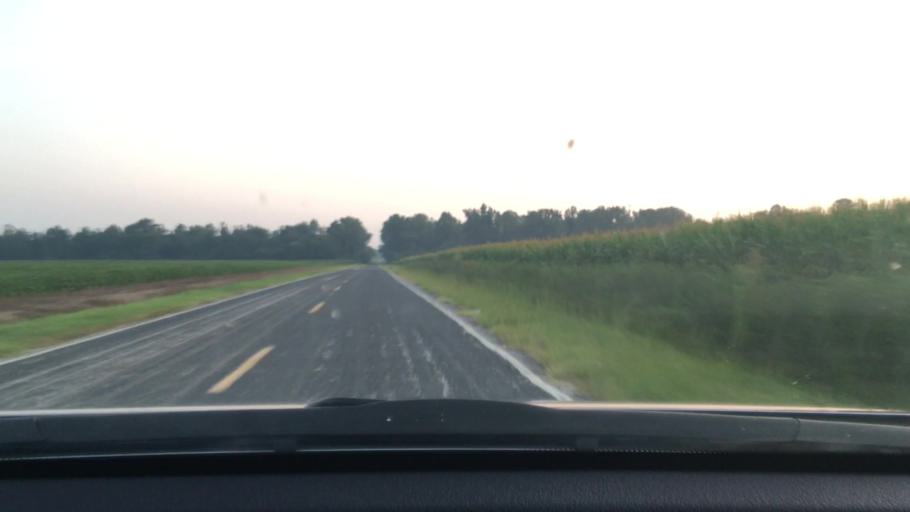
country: US
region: South Carolina
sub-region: Lee County
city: Bishopville
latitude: 34.2530
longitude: -80.1343
